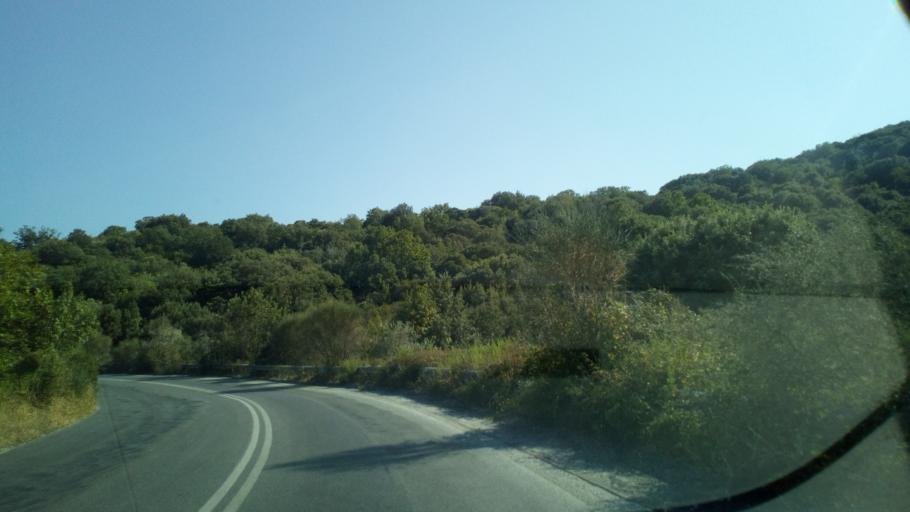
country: GR
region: Central Macedonia
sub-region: Nomos Thessalonikis
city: Stavros
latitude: 40.6186
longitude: 23.7736
